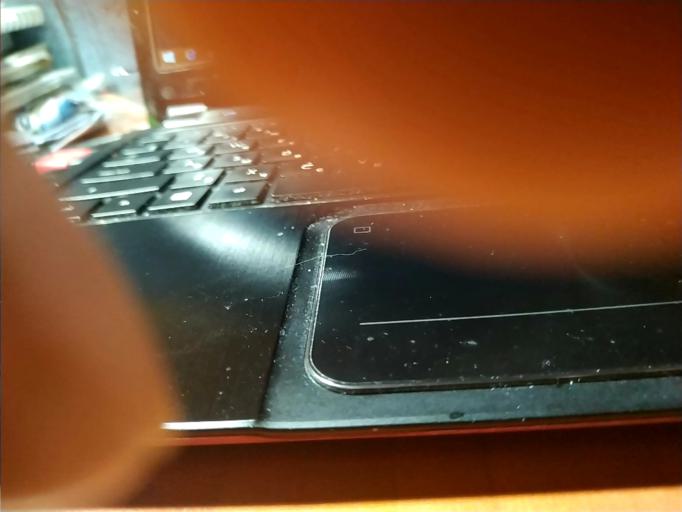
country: RU
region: Tverskaya
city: Ves'yegonsk
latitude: 58.7030
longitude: 37.5439
